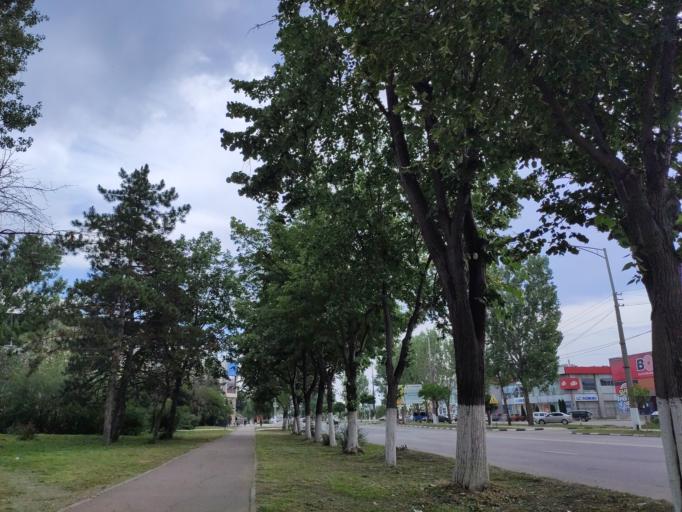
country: MD
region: Balti
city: Balti
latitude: 47.7621
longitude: 27.9409
